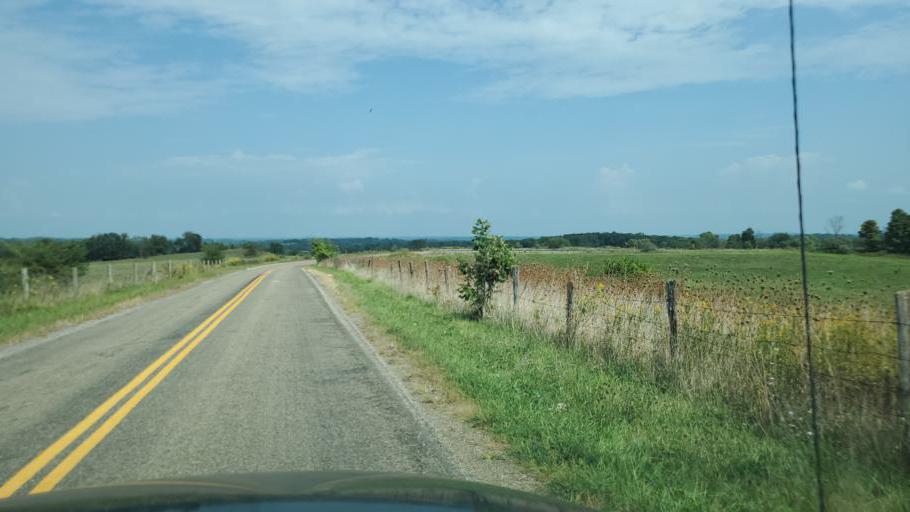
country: US
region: Ohio
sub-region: Muskingum County
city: Zanesville
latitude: 39.9400
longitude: -82.0846
